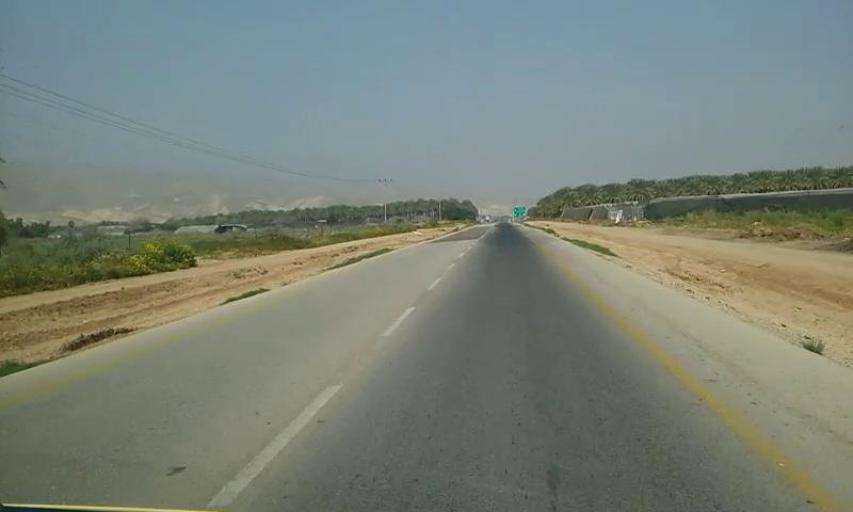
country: PS
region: West Bank
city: Al Fasayil
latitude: 31.9959
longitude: 35.4563
